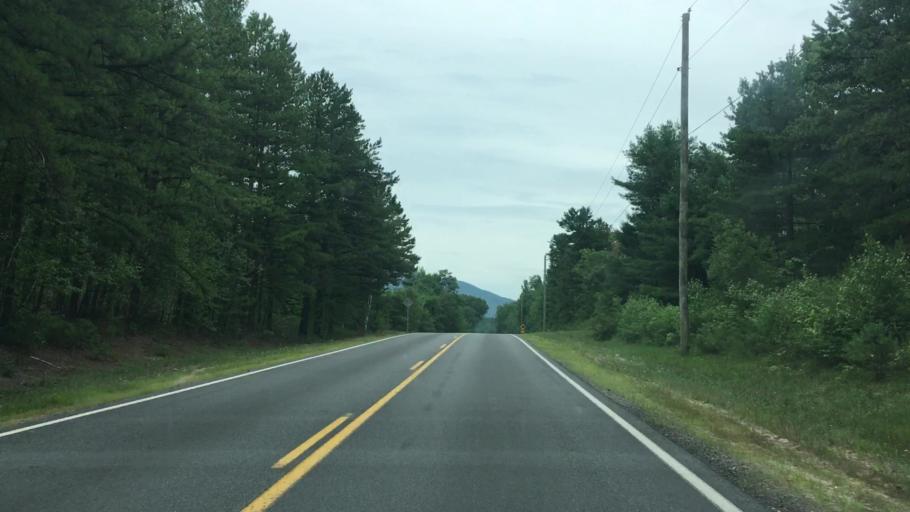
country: US
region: New York
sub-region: Essex County
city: Keeseville
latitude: 44.4703
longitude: -73.5925
